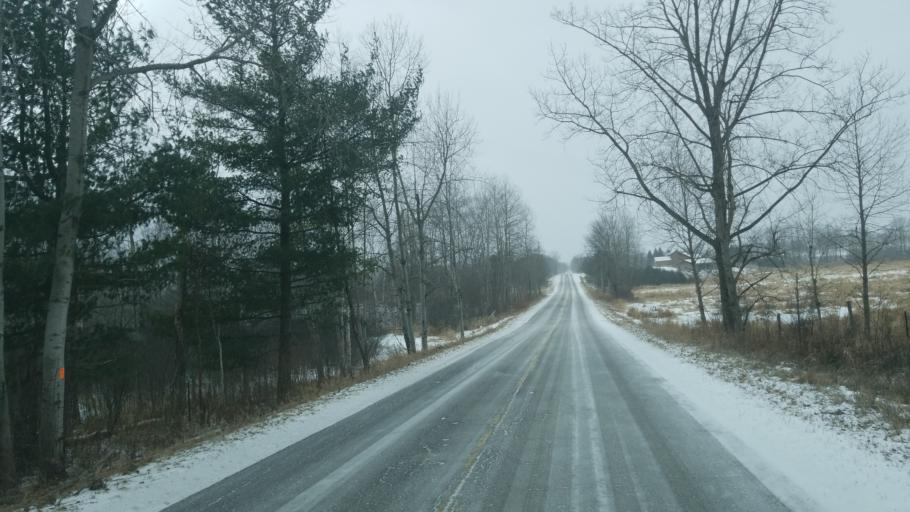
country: US
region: Michigan
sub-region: Osceola County
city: Evart
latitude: 44.0303
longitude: -85.2167
